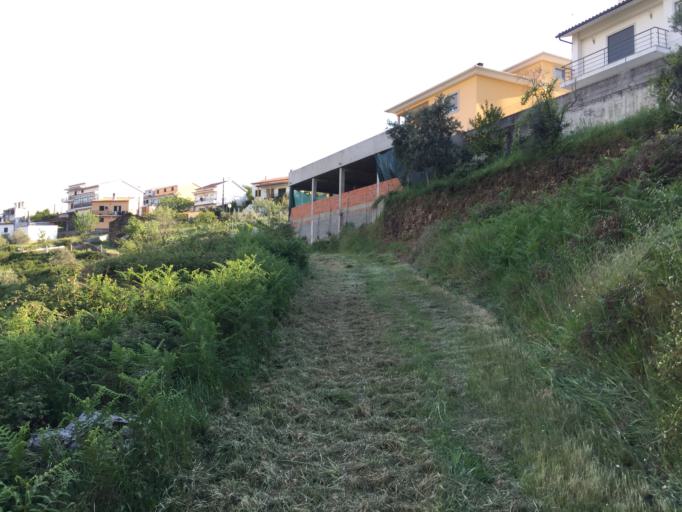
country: PT
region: Coimbra
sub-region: Pampilhosa da Serra
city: Pampilhosa da Serra
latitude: 40.1158
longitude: -7.8708
